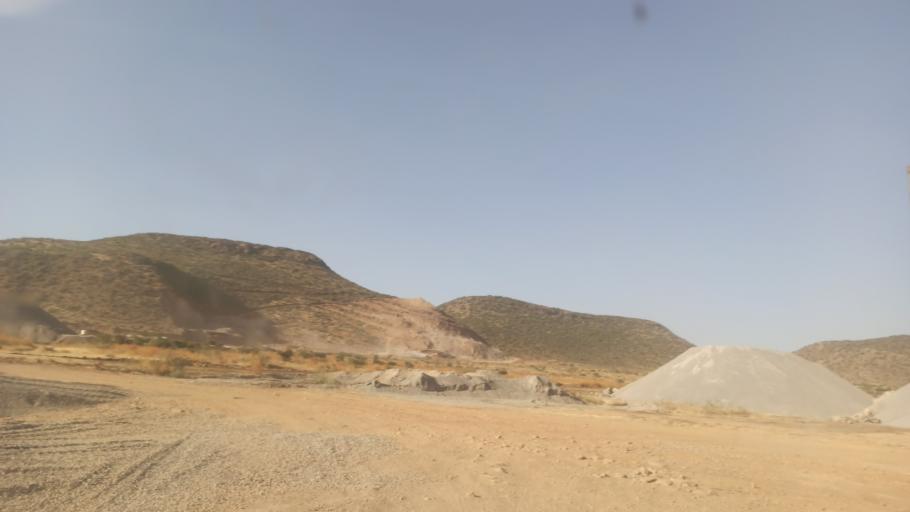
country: ET
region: Oromiya
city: Ziway
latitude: 7.9320
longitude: 38.6173
